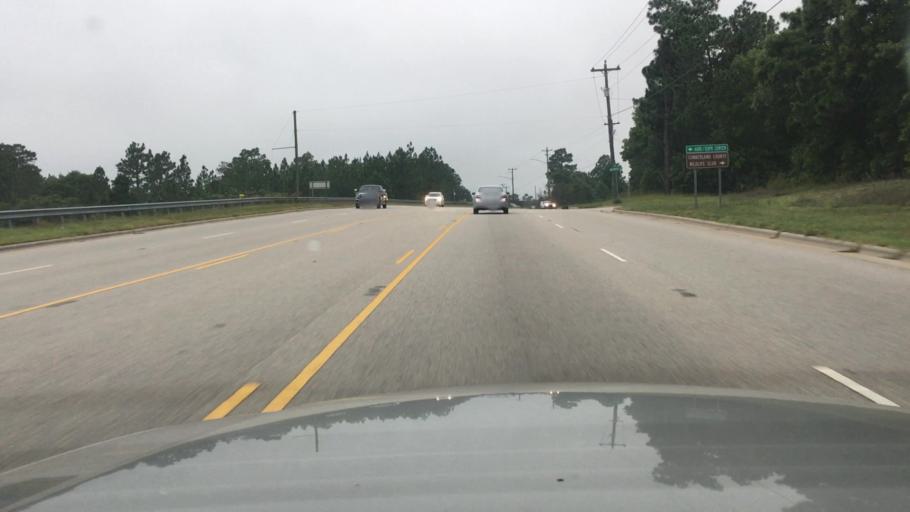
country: US
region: North Carolina
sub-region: Cumberland County
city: Fayetteville
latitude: 35.0114
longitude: -78.8859
